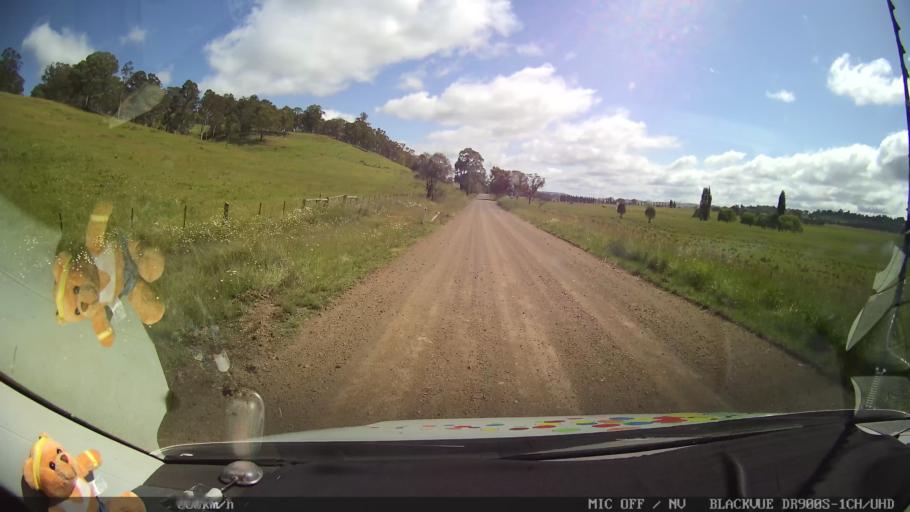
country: AU
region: New South Wales
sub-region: Glen Innes Severn
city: Glen Innes
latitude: -29.9569
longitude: 151.7028
